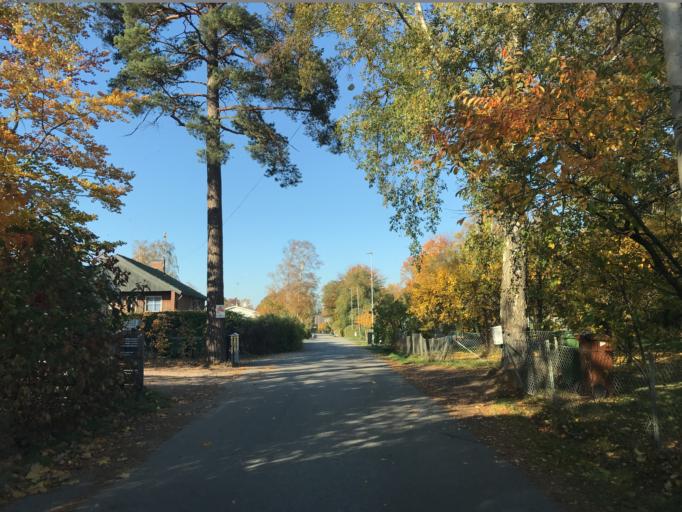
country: SE
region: Stockholm
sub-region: Sollentuna Kommun
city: Sollentuna
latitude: 59.4233
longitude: 17.9346
